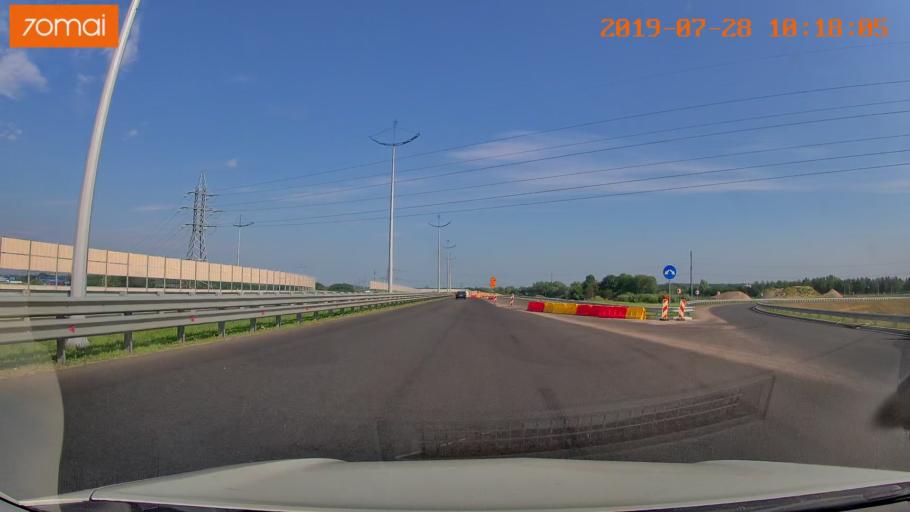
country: RU
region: Kaliningrad
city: Maloye Isakovo
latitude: 54.7472
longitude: 20.5909
